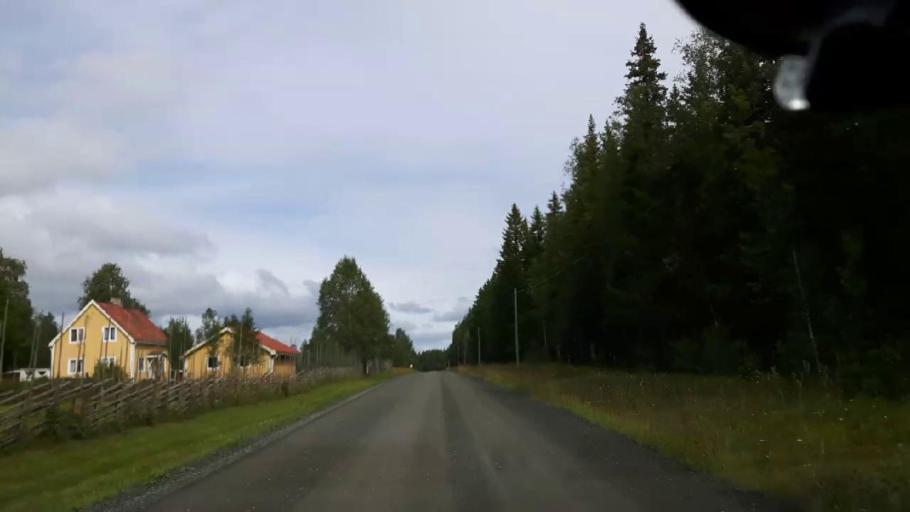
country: SE
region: Jaemtland
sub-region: Krokoms Kommun
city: Krokom
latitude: 63.3699
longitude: 14.1293
